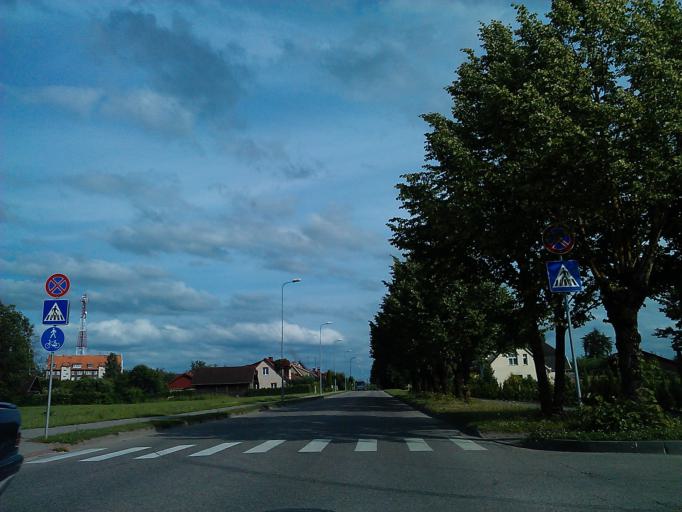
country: LV
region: Cesu Rajons
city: Cesis
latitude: 57.3053
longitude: 25.2876
